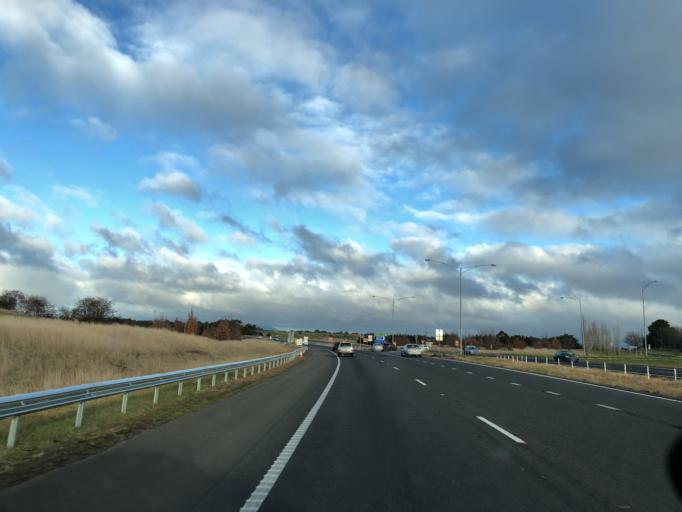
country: AU
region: Victoria
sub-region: Mount Alexander
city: Castlemaine
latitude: -37.2188
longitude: 144.4160
